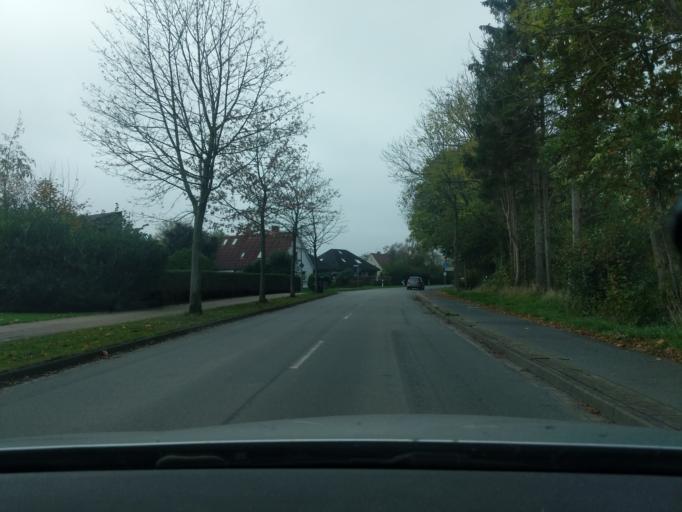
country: DE
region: Lower Saxony
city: Otterndorf
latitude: 53.8132
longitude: 8.8847
